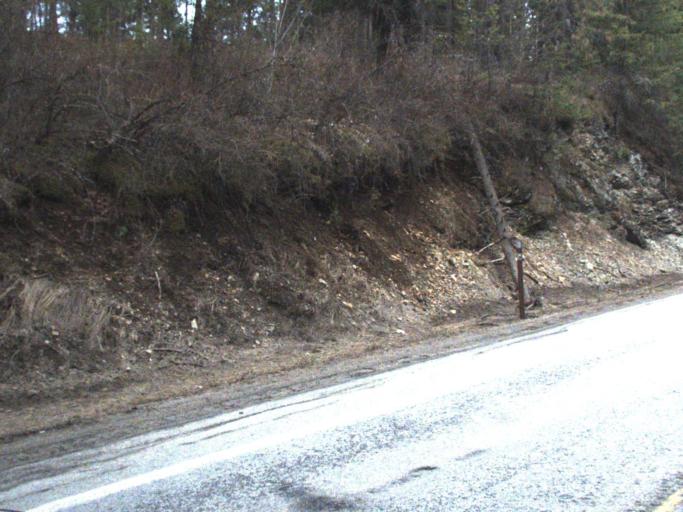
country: US
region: Washington
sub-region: Pend Oreille County
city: Newport
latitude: 48.1928
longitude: -117.0527
